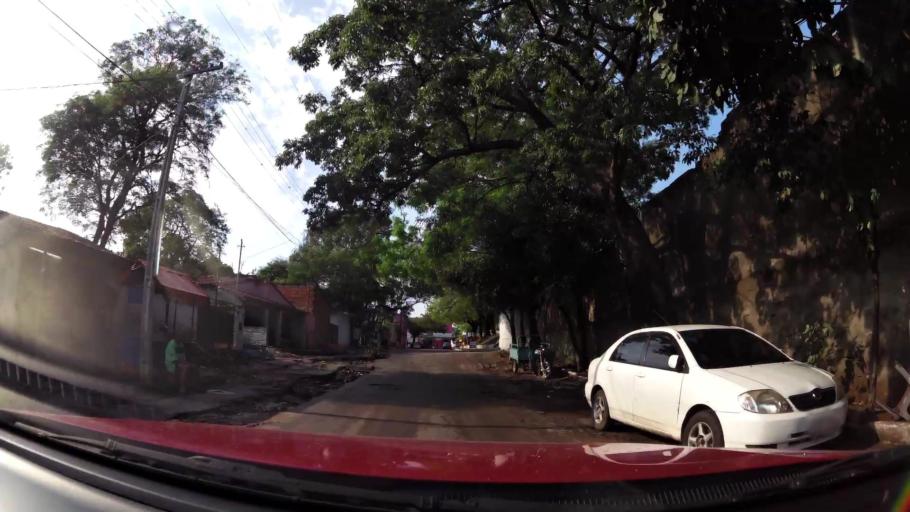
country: PY
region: Presidente Hayes
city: Nanawa
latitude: -25.2765
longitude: -57.6478
